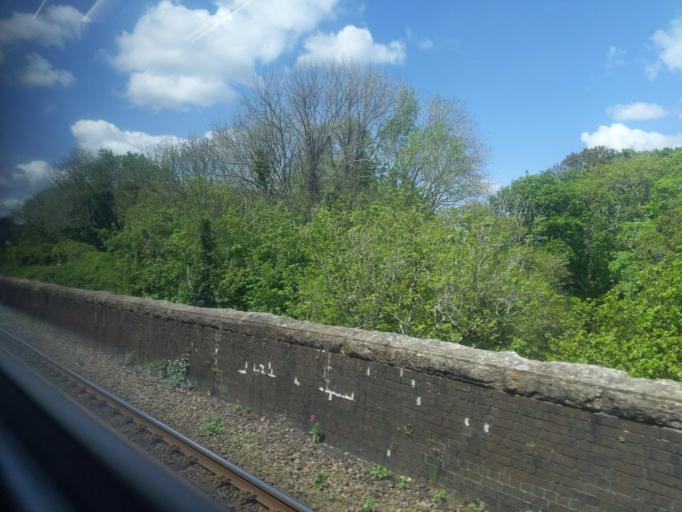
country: GB
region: England
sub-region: Cornwall
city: Pillaton
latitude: 50.3928
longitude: -4.3033
